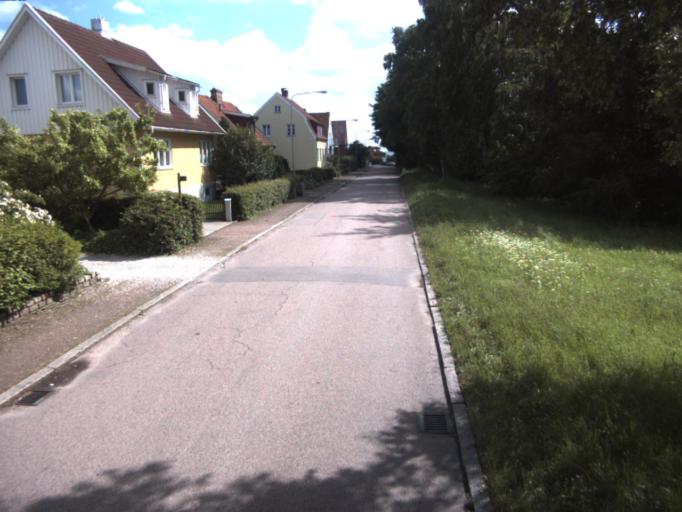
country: SE
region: Skane
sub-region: Helsingborg
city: Helsingborg
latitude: 56.0345
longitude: 12.7300
